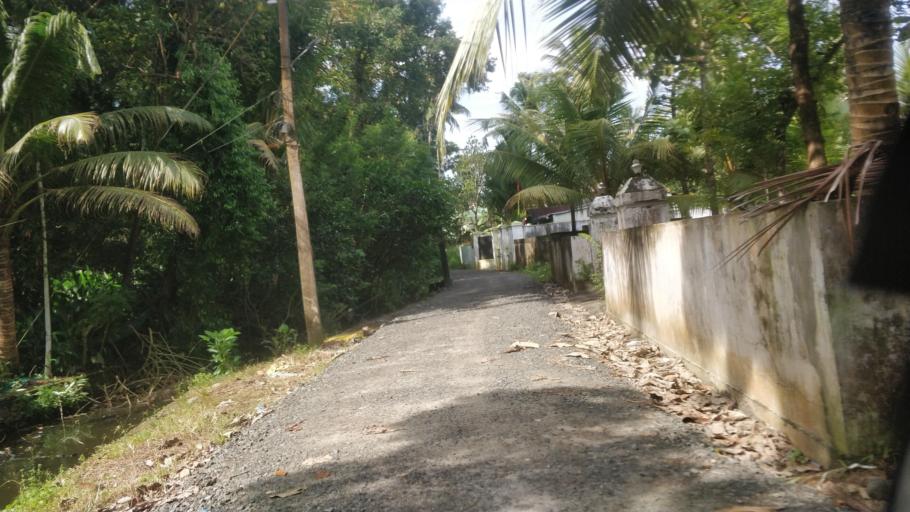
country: IN
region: Kerala
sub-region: Alappuzha
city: Vayalar
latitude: 9.6932
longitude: 76.3413
